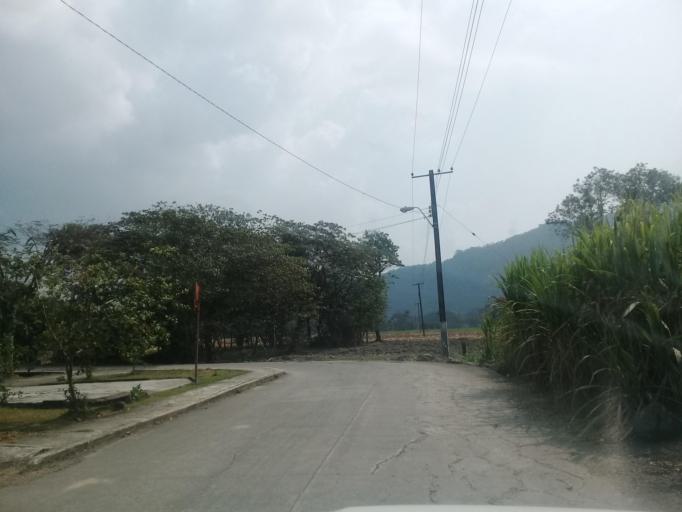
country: MX
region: Veracruz
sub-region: Ixtaczoquitlan
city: Capoluca
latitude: 18.8181
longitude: -96.9917
